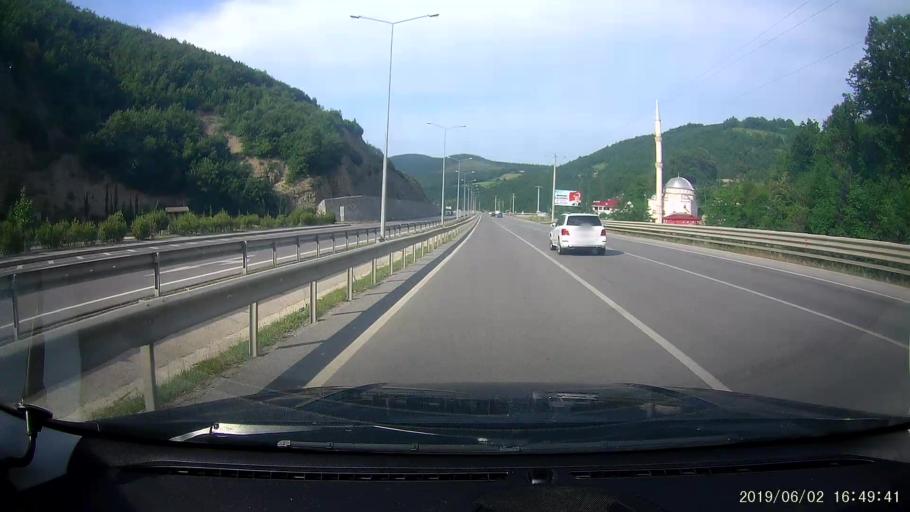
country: TR
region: Samsun
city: Samsun
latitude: 41.2411
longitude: 36.1672
